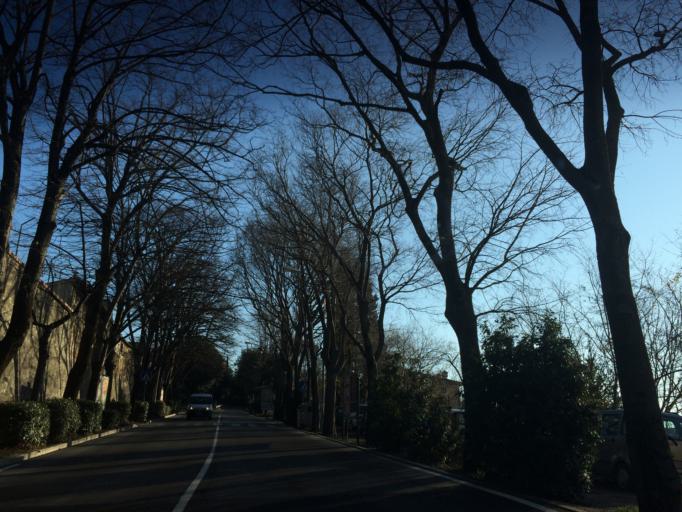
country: IT
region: Umbria
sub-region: Provincia di Perugia
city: Perugia
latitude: 43.1032
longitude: 12.3853
